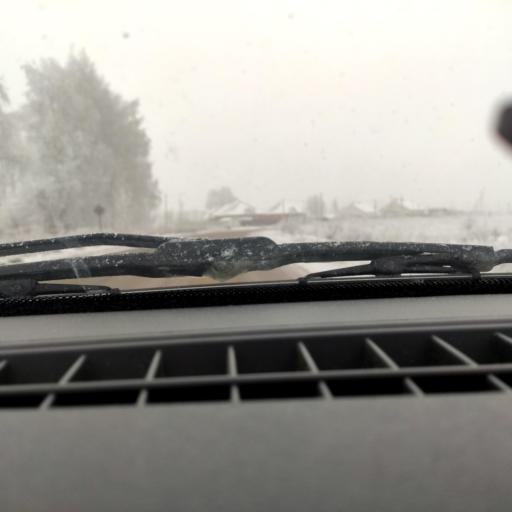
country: RU
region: Bashkortostan
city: Kabakovo
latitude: 54.6906
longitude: 56.1319
